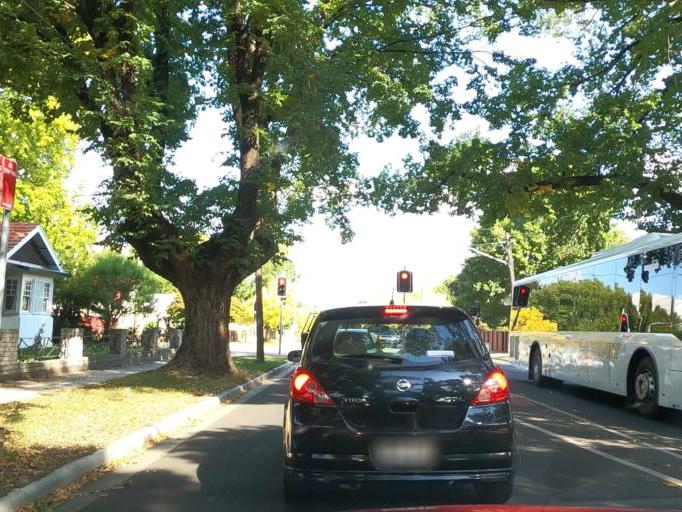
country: AU
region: New South Wales
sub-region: Albury Municipality
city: Albury
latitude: -36.0738
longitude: 146.9169
